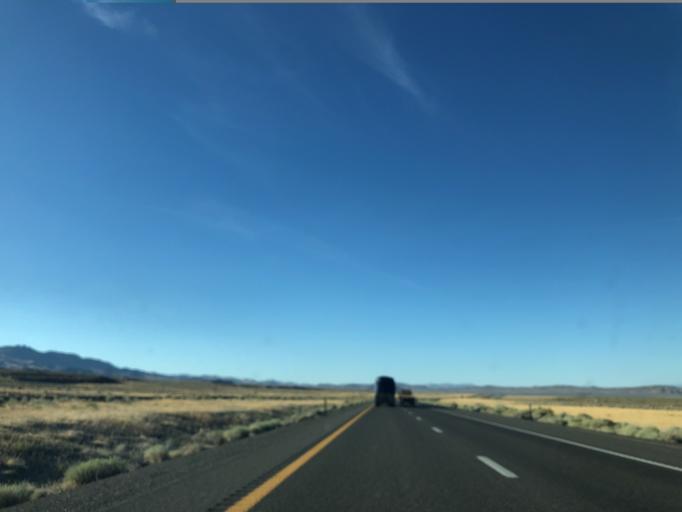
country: US
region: Nevada
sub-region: Pershing County
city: Lovelock
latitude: 40.0192
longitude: -118.6751
